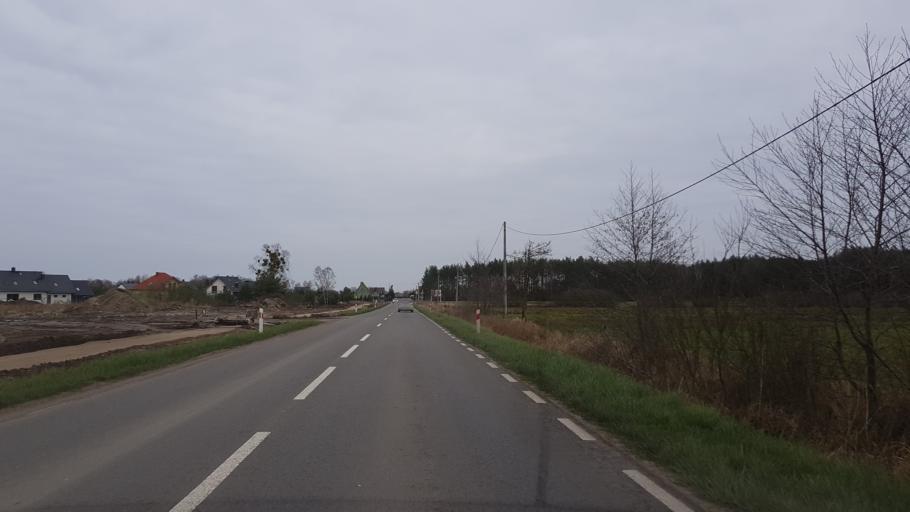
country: PL
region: West Pomeranian Voivodeship
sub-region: Powiat policki
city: Police
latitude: 53.6448
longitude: 14.5062
